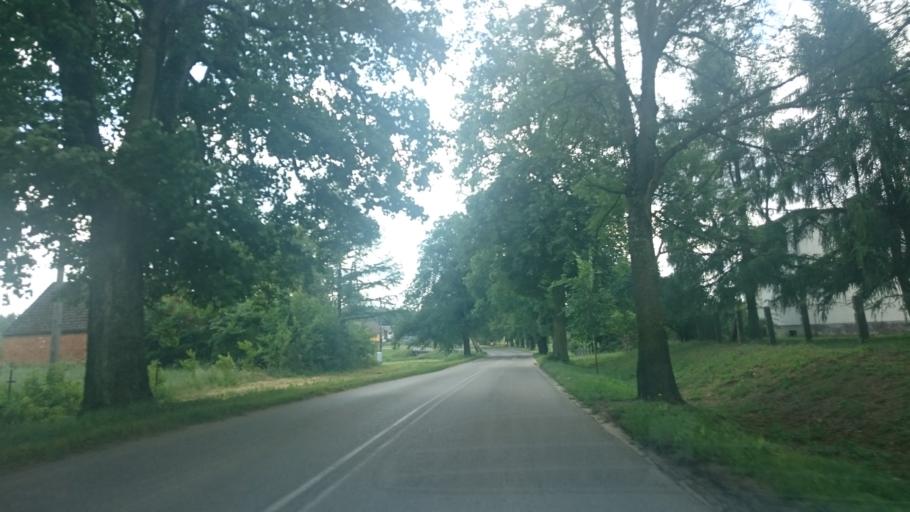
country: PL
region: Pomeranian Voivodeship
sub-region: Powiat koscierski
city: Stara Kiszewa
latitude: 53.9774
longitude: 18.2284
